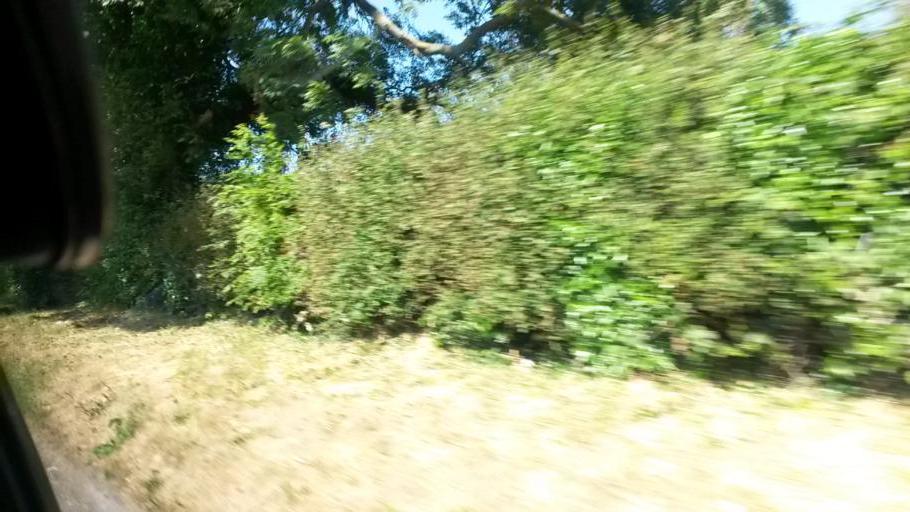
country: IE
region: Leinster
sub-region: Fingal County
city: Swords
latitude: 53.4944
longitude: -6.2694
